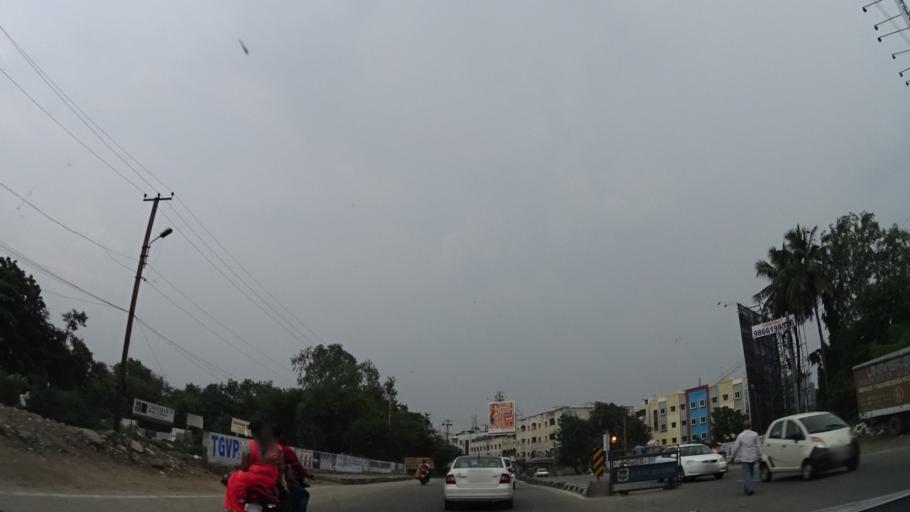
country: IN
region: Telangana
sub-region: Rangareddi
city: Quthbullapur
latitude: 17.4584
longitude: 78.4777
